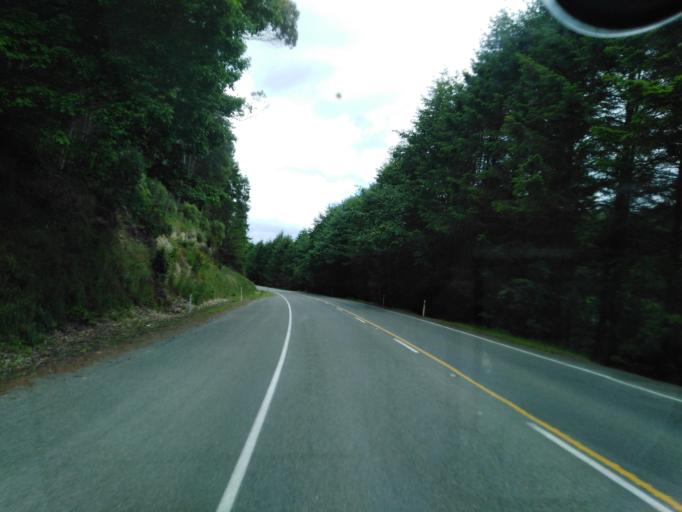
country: NZ
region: Tasman
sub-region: Tasman District
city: Wakefield
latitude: -41.4785
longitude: 172.8746
